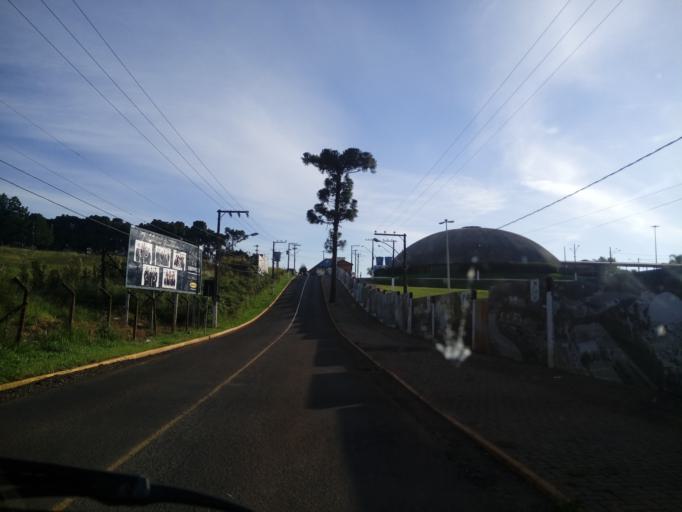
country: BR
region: Santa Catarina
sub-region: Chapeco
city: Chapeco
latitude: -27.0962
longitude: -52.6626
